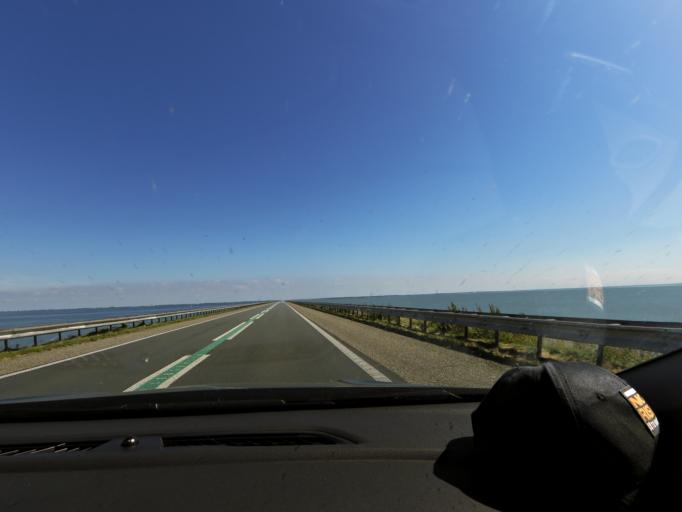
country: NL
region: Flevoland
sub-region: Gemeente Lelystad
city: Lelystad
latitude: 52.6297
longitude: 5.4192
